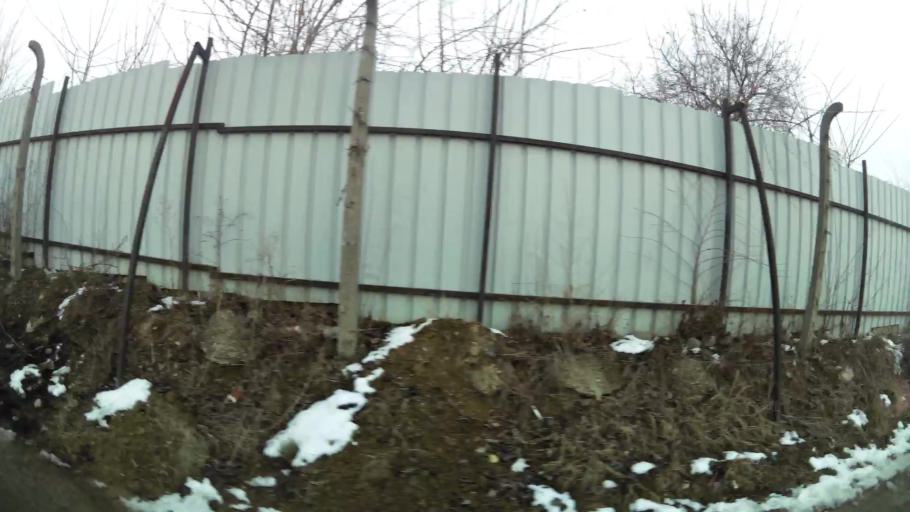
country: MK
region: Suto Orizari
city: Suto Orizare
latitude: 42.0361
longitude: 21.4326
